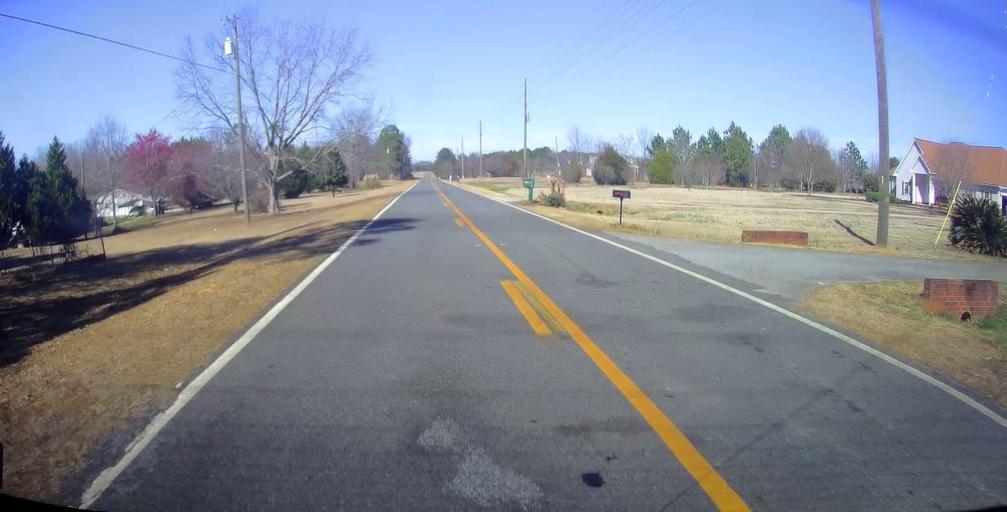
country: US
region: Georgia
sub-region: Peach County
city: Byron
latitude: 32.6326
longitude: -83.7671
